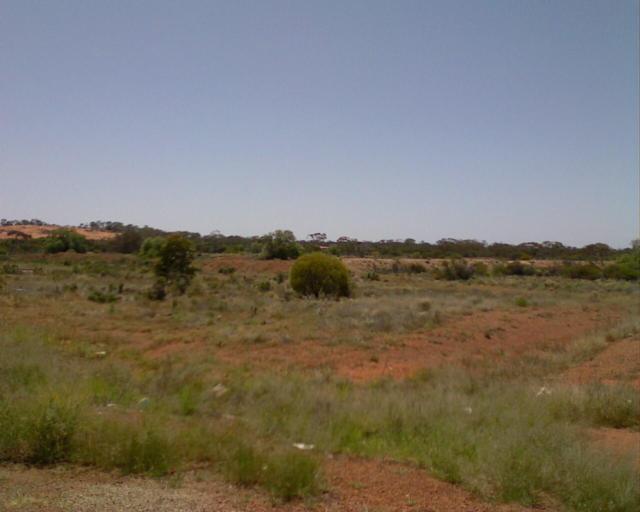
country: AU
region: Western Australia
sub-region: Kalgoorlie/Boulder
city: Kalgoorlie
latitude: -31.0126
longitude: 120.8687
